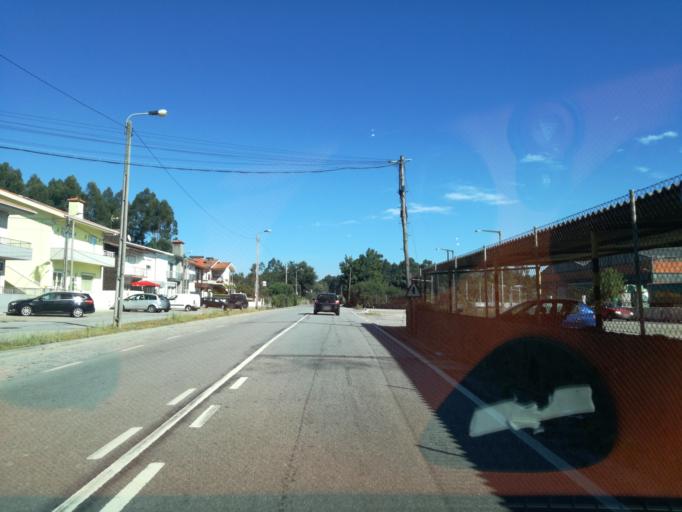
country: PT
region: Porto
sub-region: Trofa
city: Sao Romao do Coronado
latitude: 41.2855
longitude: -8.5926
